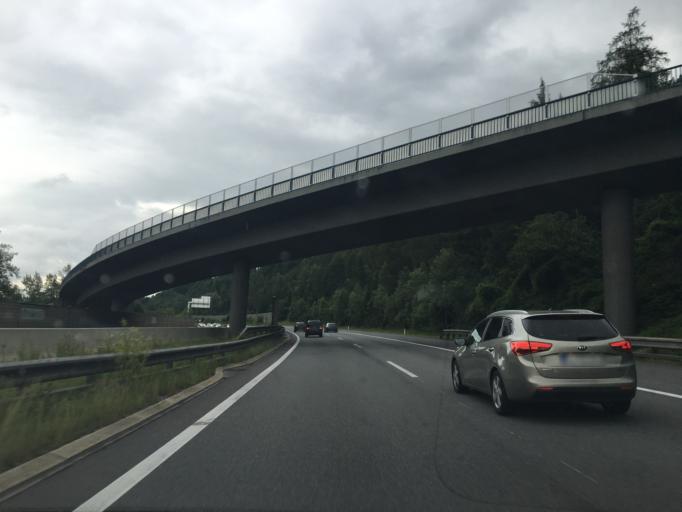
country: AT
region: Tyrol
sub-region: Politischer Bezirk Innsbruck Land
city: Rinn
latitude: 47.2717
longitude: 11.4949
